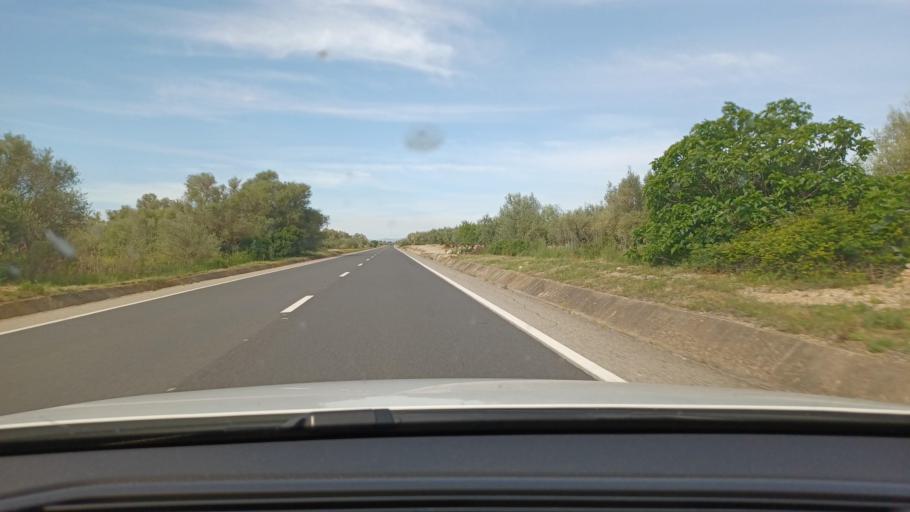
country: ES
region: Catalonia
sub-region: Provincia de Tarragona
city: Ulldecona
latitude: 40.6579
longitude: 0.4099
